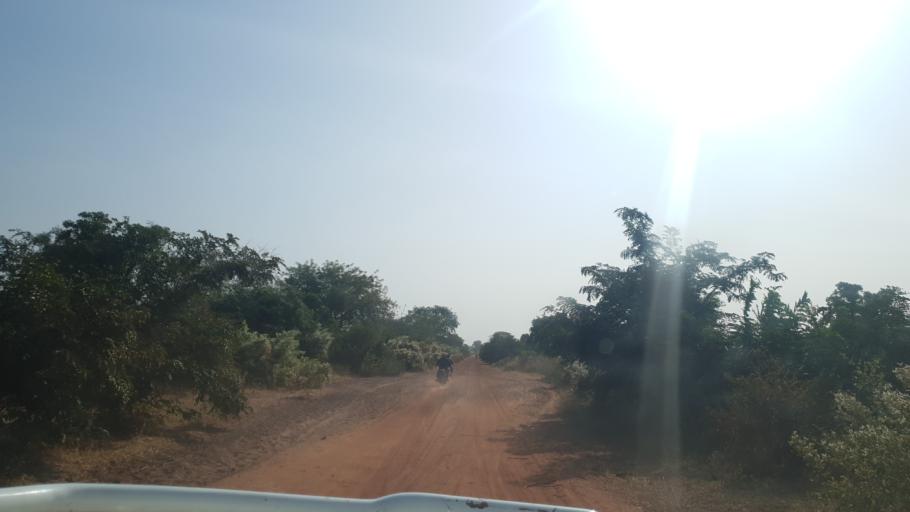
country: ML
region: Koulikoro
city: Dioila
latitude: 12.7092
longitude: -6.7823
